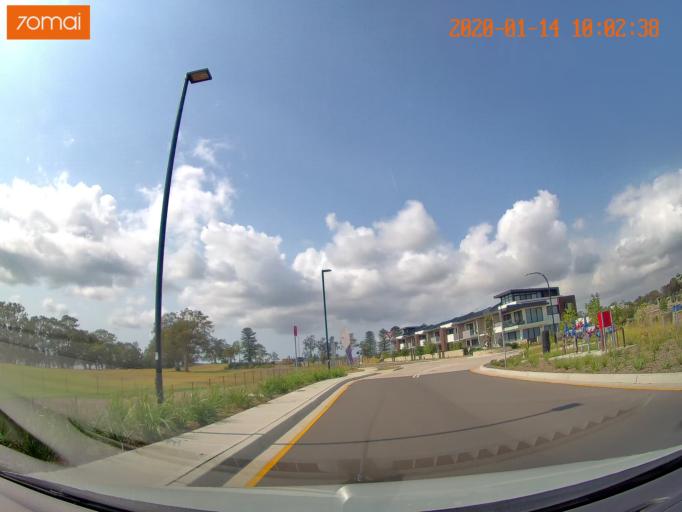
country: AU
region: New South Wales
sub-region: Wyong Shire
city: Kingfisher Shores
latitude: -33.1234
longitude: 151.5405
